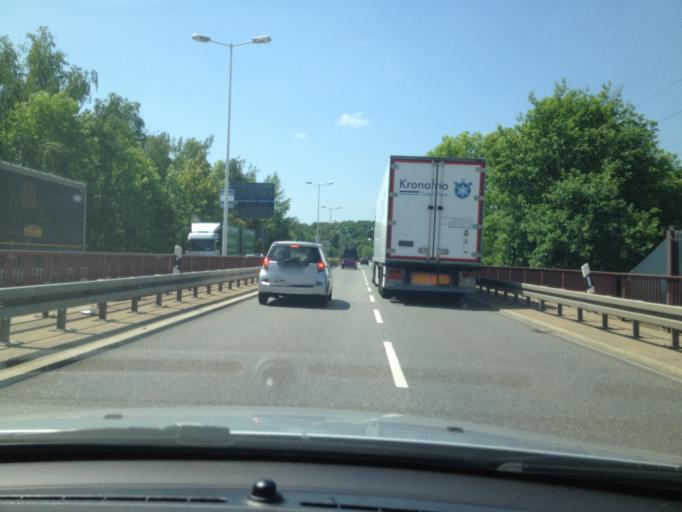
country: DE
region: Saxony
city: Chemnitz
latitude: 50.7984
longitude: 12.9142
